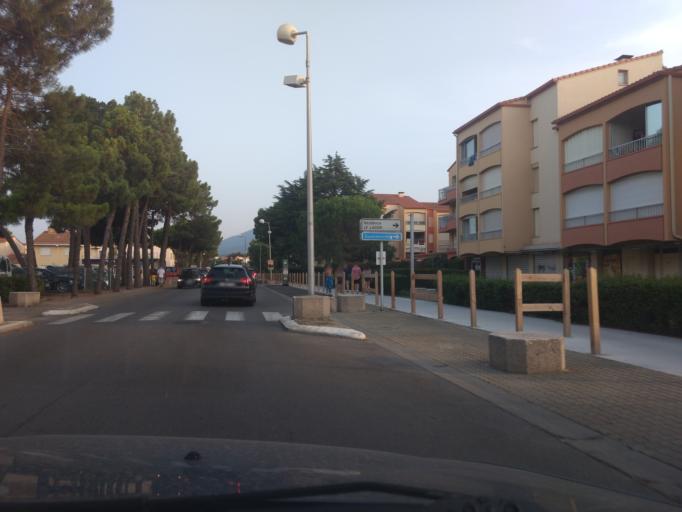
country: FR
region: Languedoc-Roussillon
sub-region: Departement des Pyrenees-Orientales
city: Argelers
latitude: 42.5602
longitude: 3.0412
